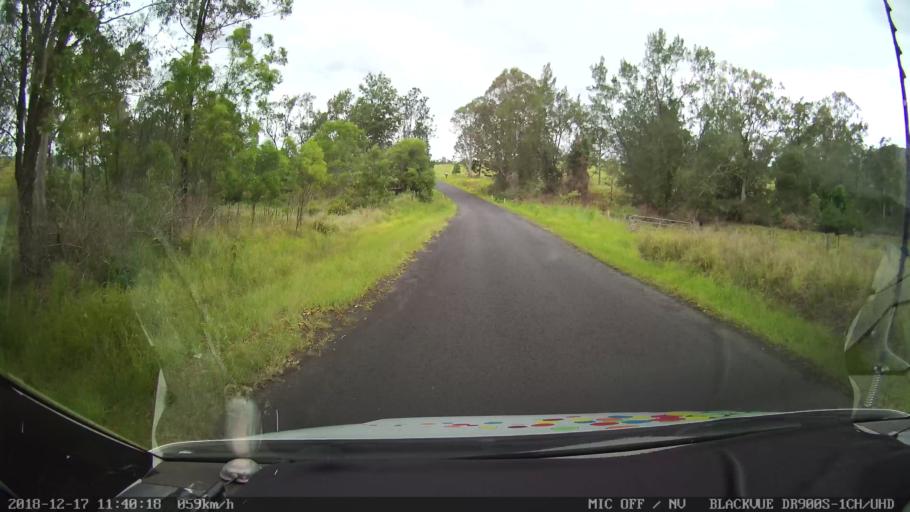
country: AU
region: New South Wales
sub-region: Kyogle
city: Kyogle
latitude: -28.6835
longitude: 152.5932
